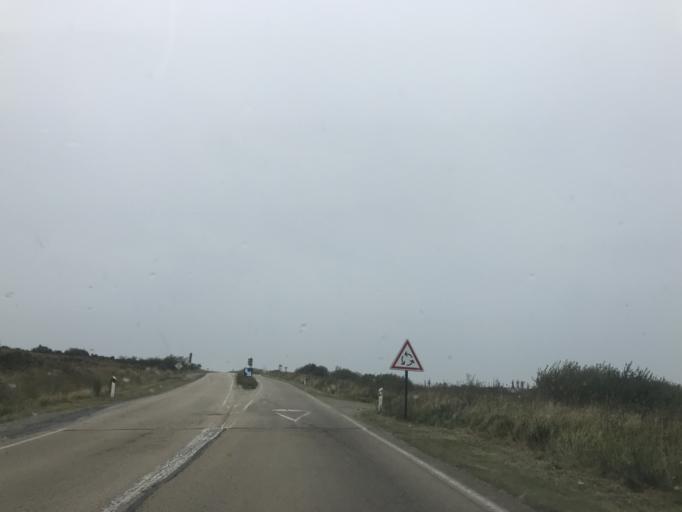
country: FR
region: Brittany
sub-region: Departement du Finistere
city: Plouneour-Menez
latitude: 48.4136
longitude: -3.8949
